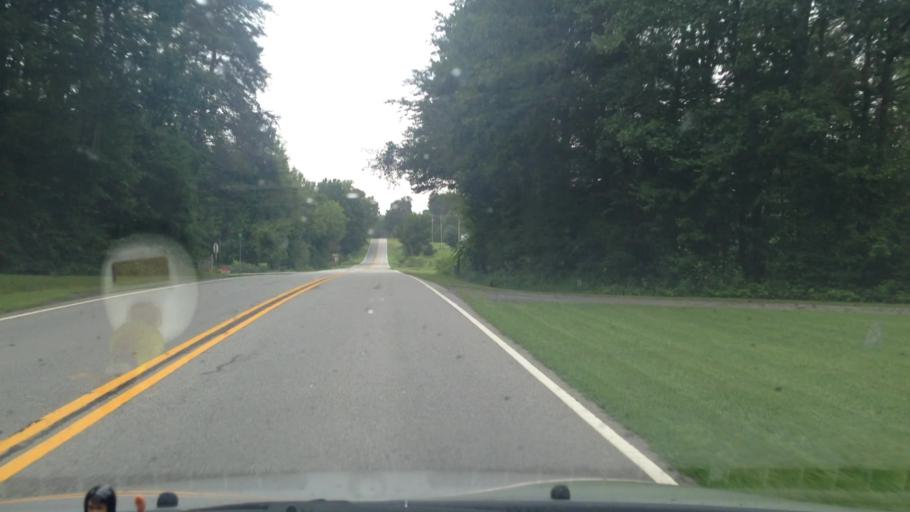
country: US
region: North Carolina
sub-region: Stokes County
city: Danbury
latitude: 36.3976
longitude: -80.1416
